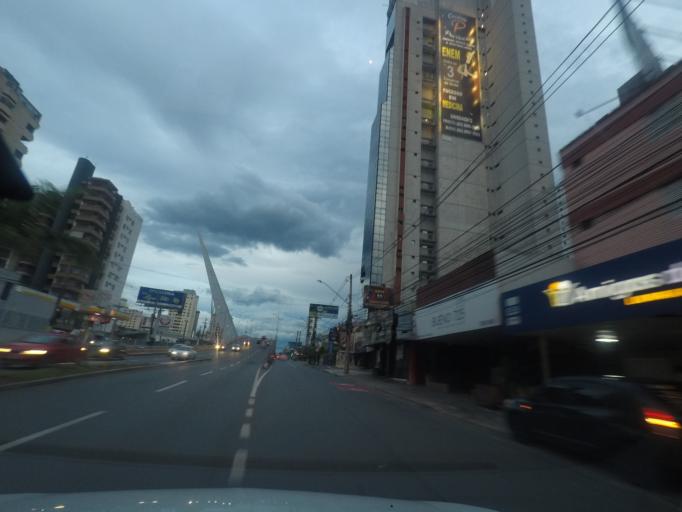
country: BR
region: Goias
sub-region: Goiania
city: Goiania
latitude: -16.7140
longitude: -49.2655
